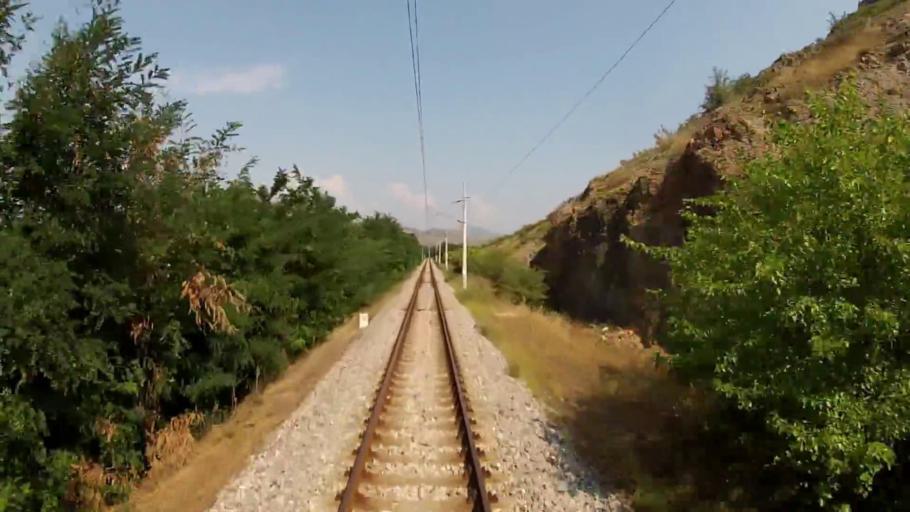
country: BG
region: Blagoevgrad
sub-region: Obshtina Sandanski
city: Sandanski
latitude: 41.4916
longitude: 23.2683
